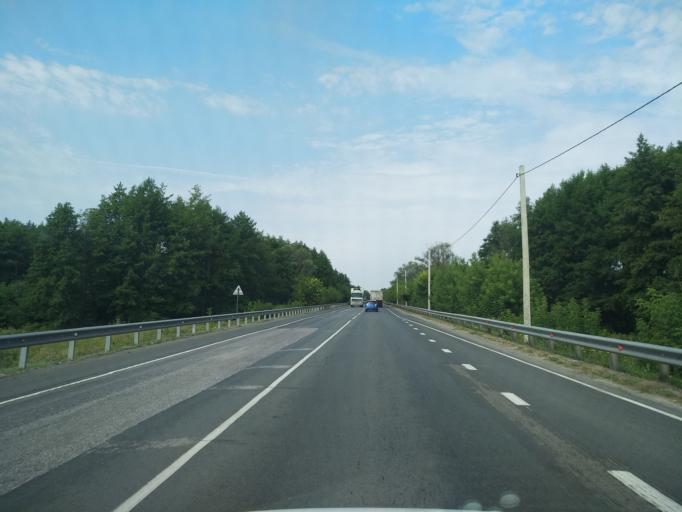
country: RU
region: Voronezj
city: Orlovo
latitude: 51.6809
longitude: 39.5971
